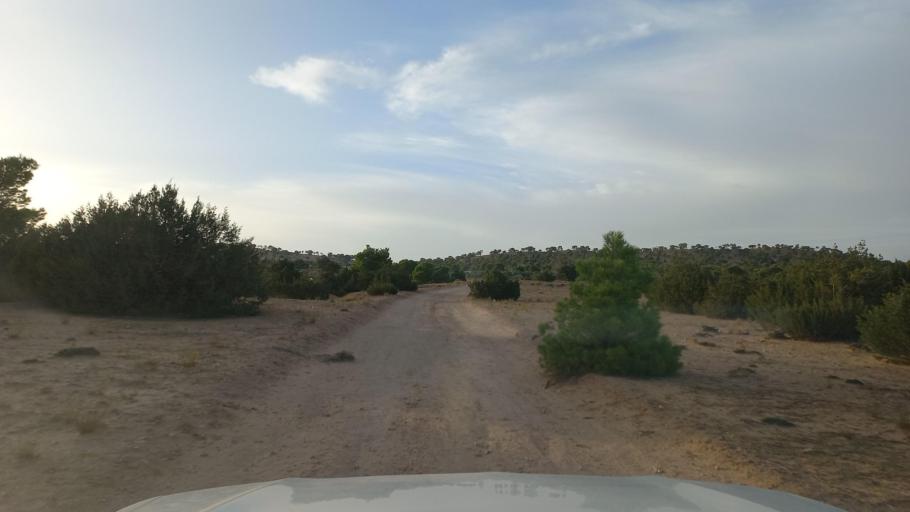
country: TN
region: Al Qasrayn
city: Sbiba
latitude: 35.4098
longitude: 8.9166
